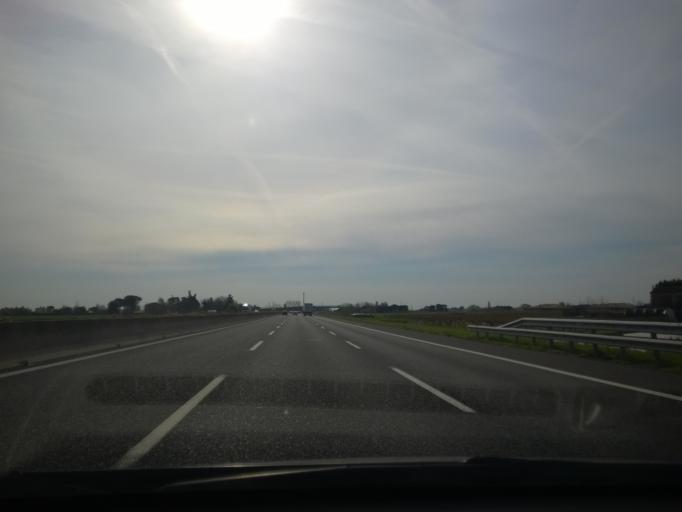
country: IT
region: Emilia-Romagna
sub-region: Forli-Cesena
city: Bagnarola
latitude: 44.1616
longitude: 12.3036
